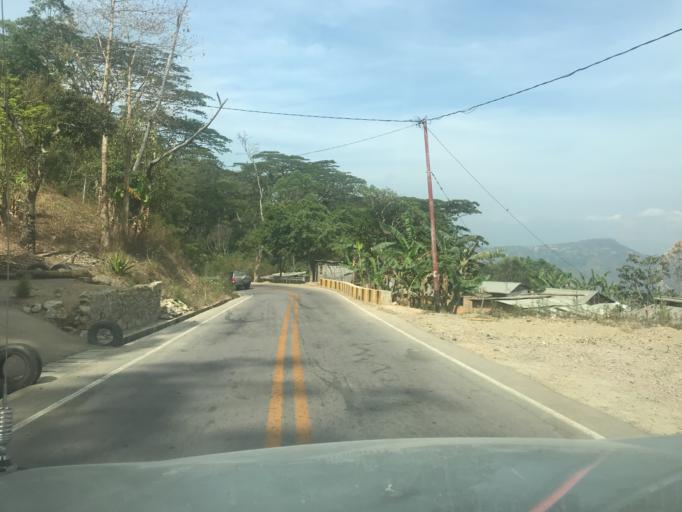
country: TL
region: Aileu
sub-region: Aileu Villa
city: Aileu
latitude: -8.6727
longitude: 125.5558
